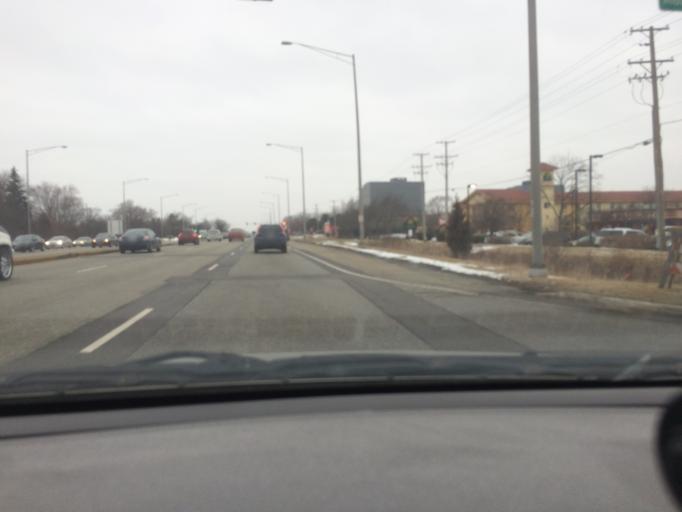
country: US
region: Illinois
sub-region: Cook County
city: Hoffman Estates
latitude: 42.0381
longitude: -88.0356
